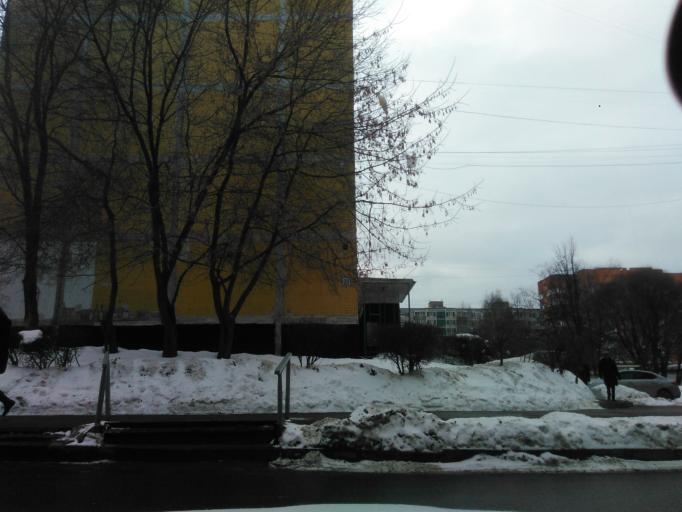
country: RU
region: Moskovskaya
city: Andreyevka
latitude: 55.9770
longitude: 37.1444
